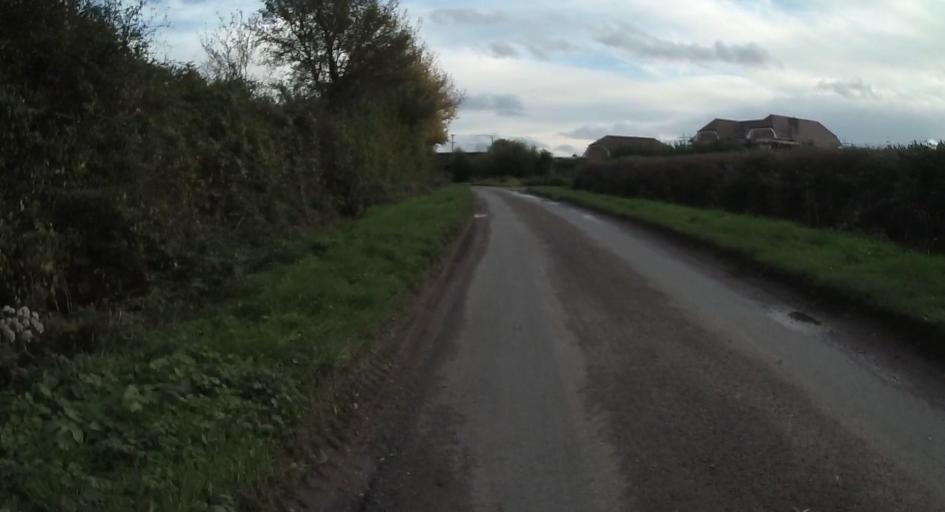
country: GB
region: England
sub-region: Wokingham
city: Swallowfield
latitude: 51.3711
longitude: -0.9593
